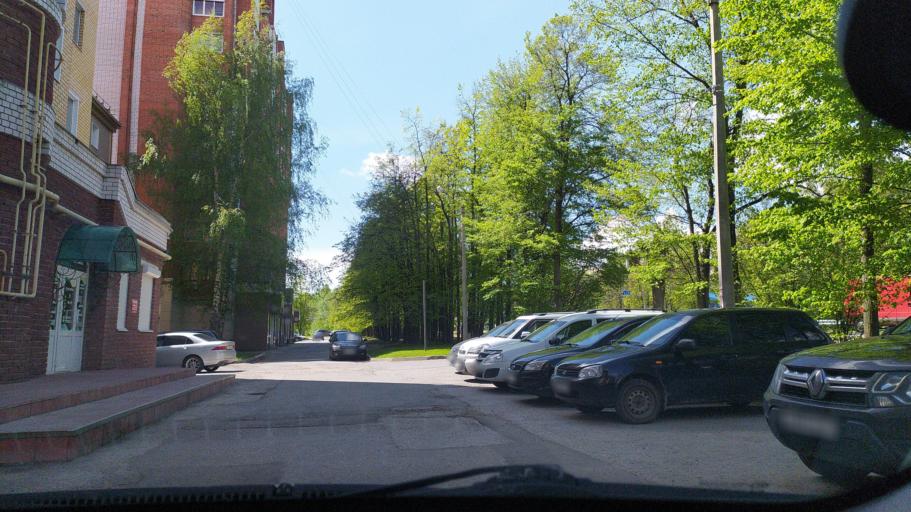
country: RU
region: Chuvashia
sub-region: Cheboksarskiy Rayon
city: Cheboksary
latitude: 56.1413
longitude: 47.2007
